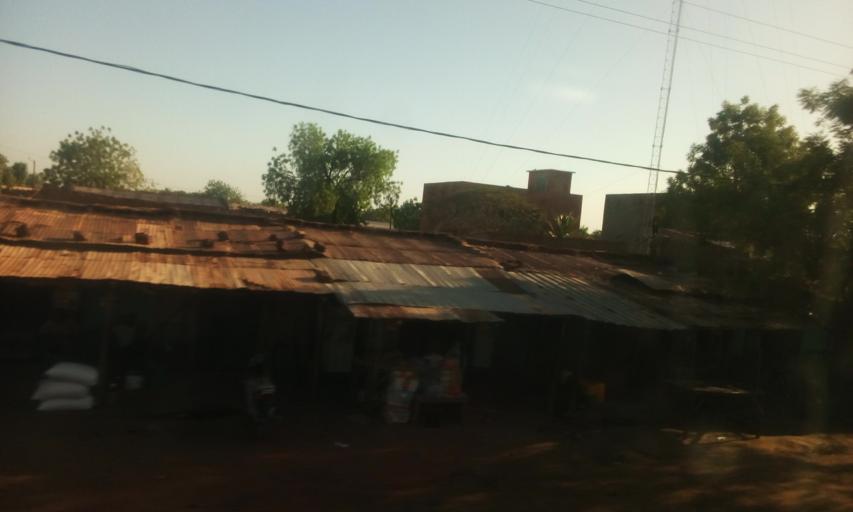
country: ML
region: Segou
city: Baroueli
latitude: 12.7837
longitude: -6.9518
